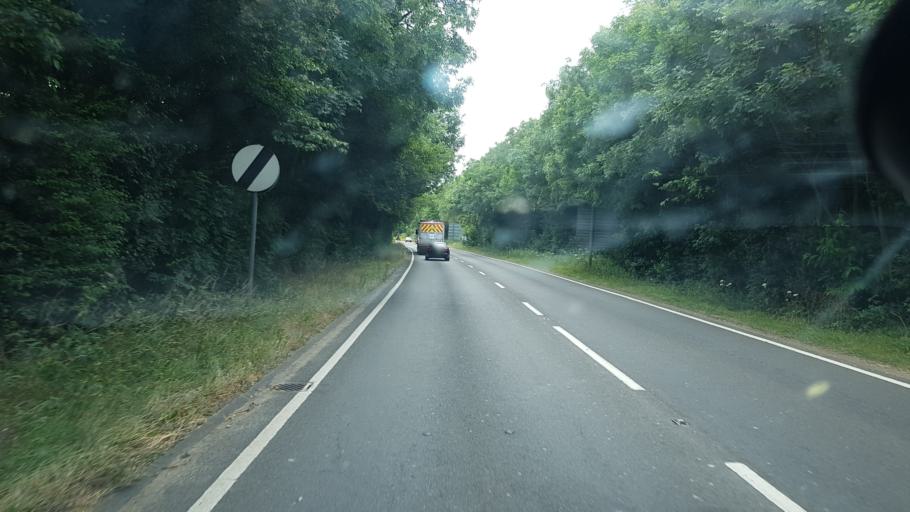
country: GB
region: England
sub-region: Surrey
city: Godstone
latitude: 51.2488
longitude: -0.0527
